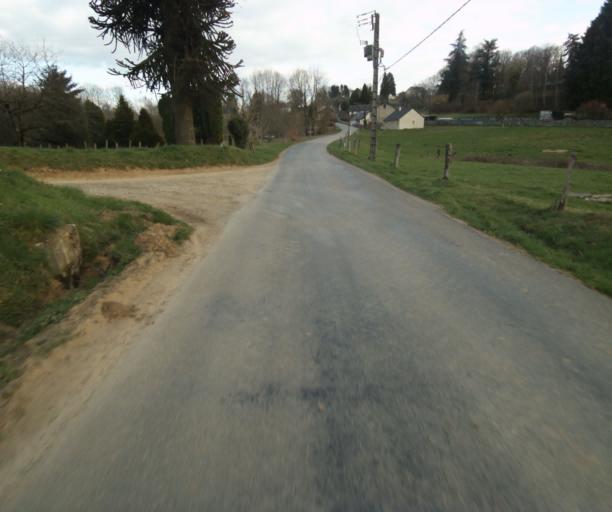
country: FR
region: Limousin
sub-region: Departement de la Correze
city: Saint-Clement
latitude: 45.3564
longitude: 1.6321
